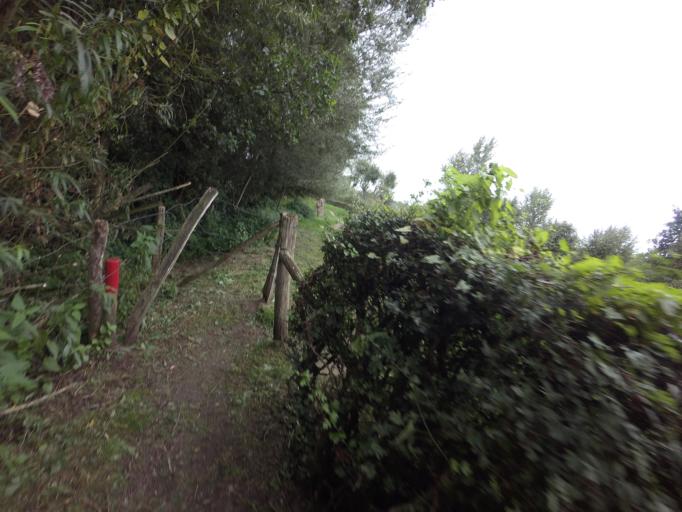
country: NL
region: Limburg
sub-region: Valkenburg aan de Geul
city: Schin op Geul
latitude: 50.8504
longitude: 5.8760
